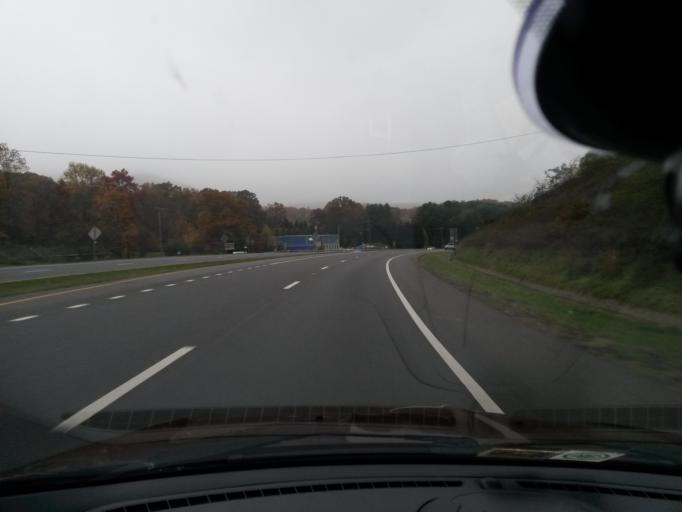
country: US
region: Virginia
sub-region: Botetourt County
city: Cloverdale
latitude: 37.3763
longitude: -79.8874
